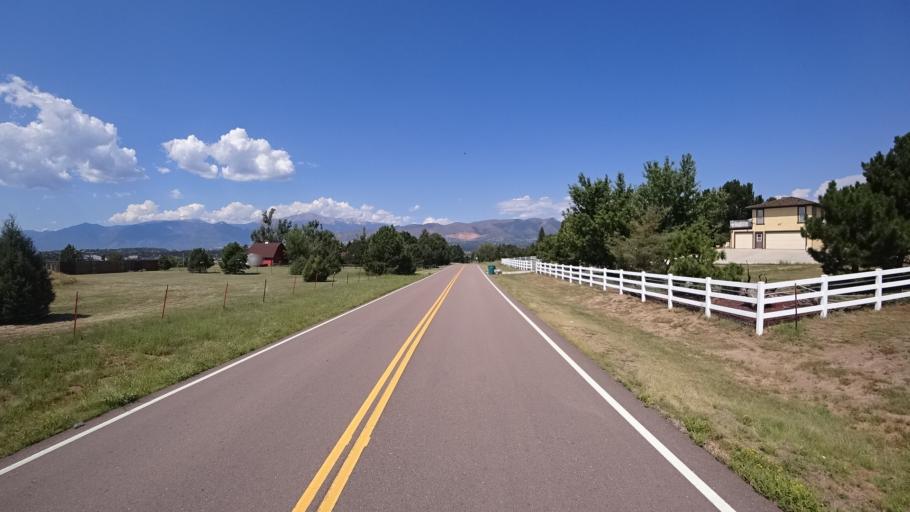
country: US
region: Colorado
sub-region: El Paso County
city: Air Force Academy
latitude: 38.9356
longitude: -104.7780
